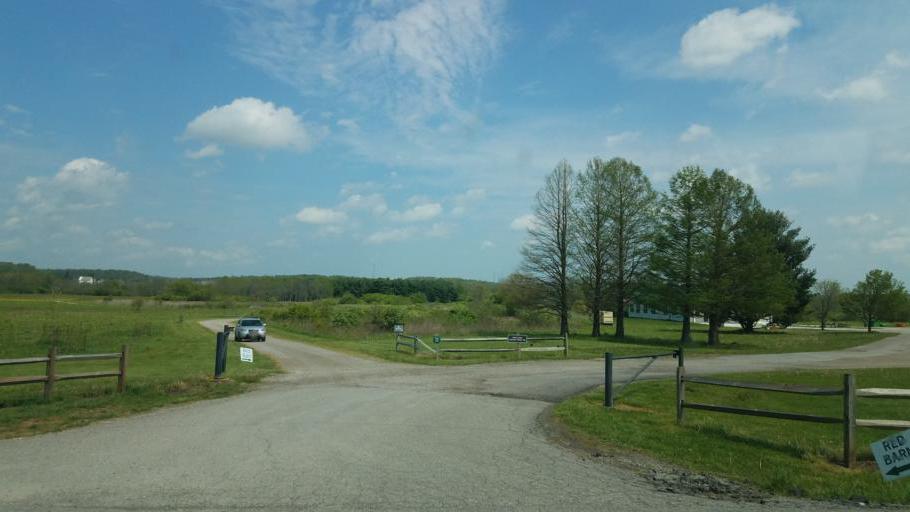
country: US
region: Ohio
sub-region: Licking County
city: Heath
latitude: 39.9857
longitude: -82.4134
